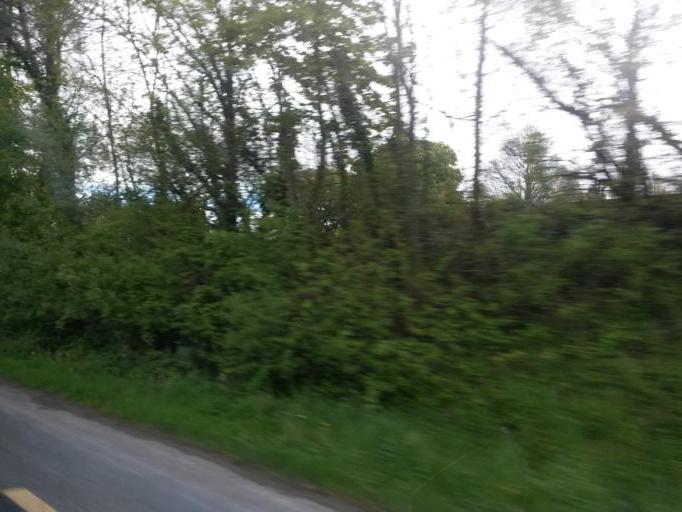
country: IE
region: Leinster
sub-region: Loch Garman
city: Enniscorthy
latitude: 52.4906
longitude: -6.5657
